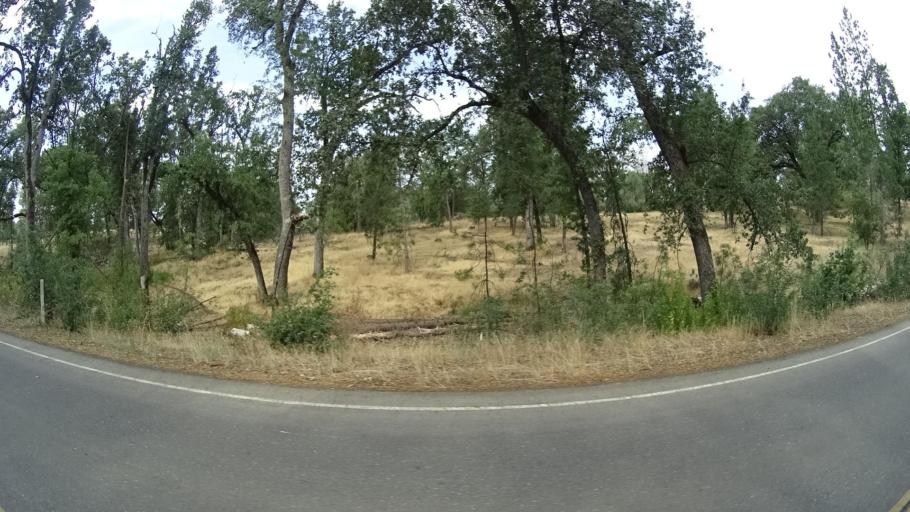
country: US
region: California
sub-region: Mariposa County
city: Midpines
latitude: 37.5291
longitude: -119.9477
